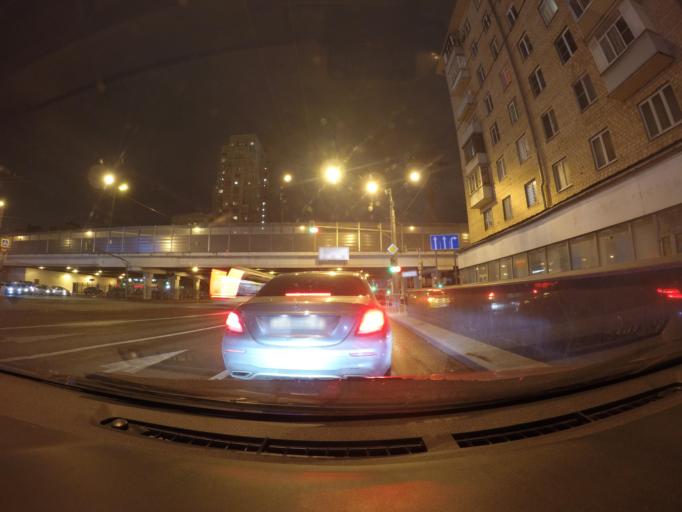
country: RU
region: Moscow
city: Sokol'niki
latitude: 55.7810
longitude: 37.6691
